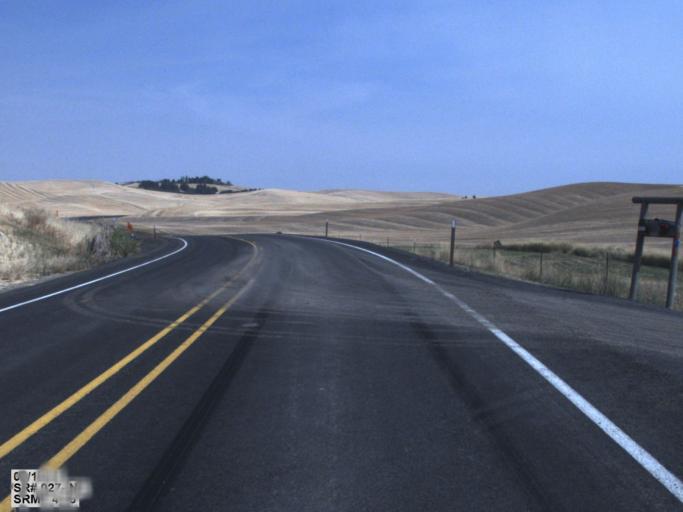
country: US
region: Washington
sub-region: Whitman County
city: Pullman
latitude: 46.7854
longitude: -117.1486
